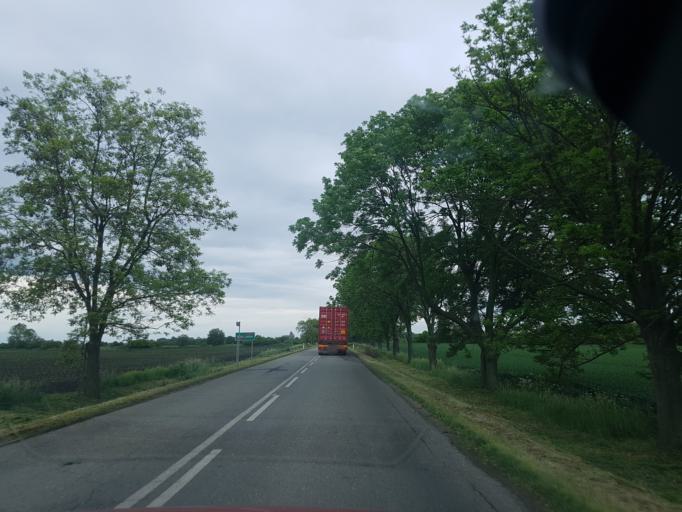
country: PL
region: Lower Silesian Voivodeship
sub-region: Powiat wroclawski
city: Kobierzyce
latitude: 50.9422
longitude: 16.9243
